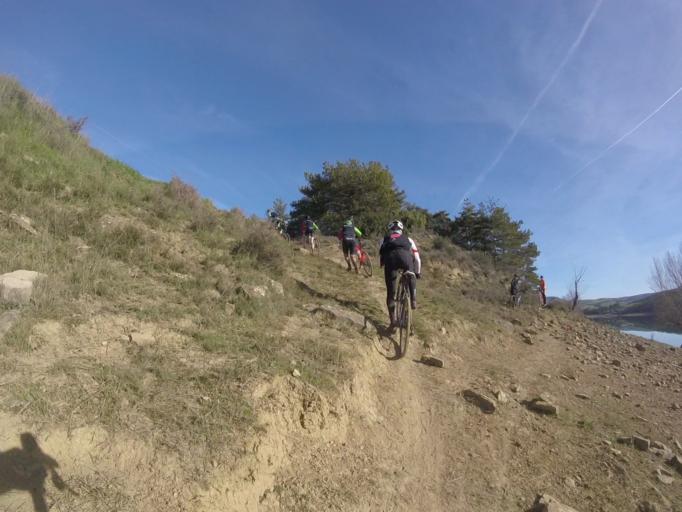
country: ES
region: Navarre
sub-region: Provincia de Navarra
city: Yerri
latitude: 42.7108
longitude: -1.9538
